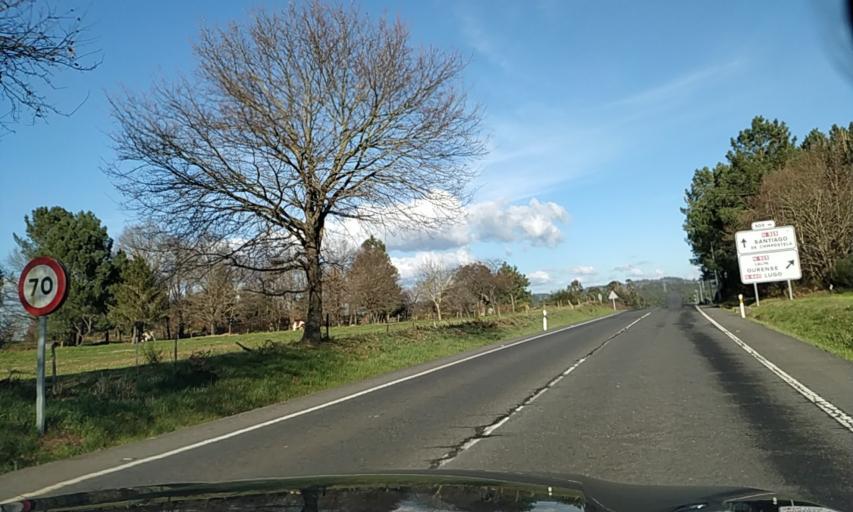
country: ES
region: Galicia
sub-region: Provincia de Pontevedra
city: Silleda
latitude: 42.7148
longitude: -8.2914
